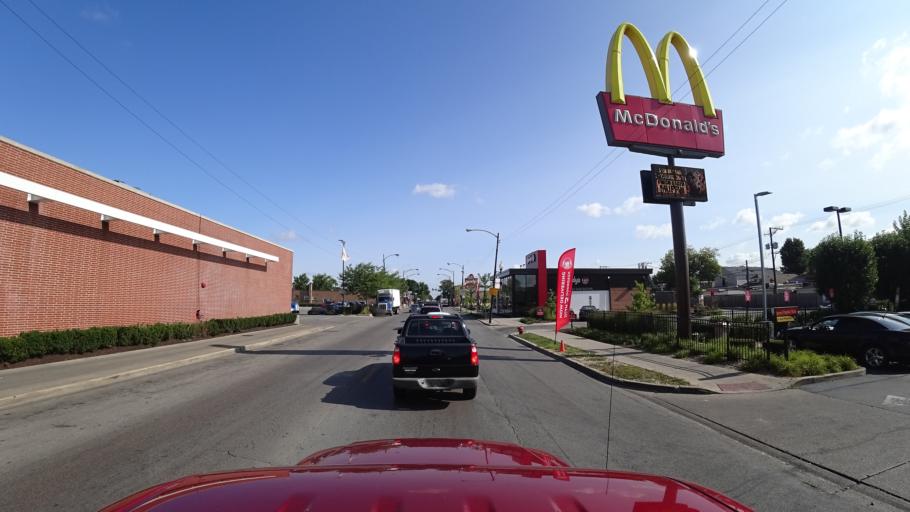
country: US
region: Illinois
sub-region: Cook County
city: Hometown
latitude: 41.7888
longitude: -87.7034
